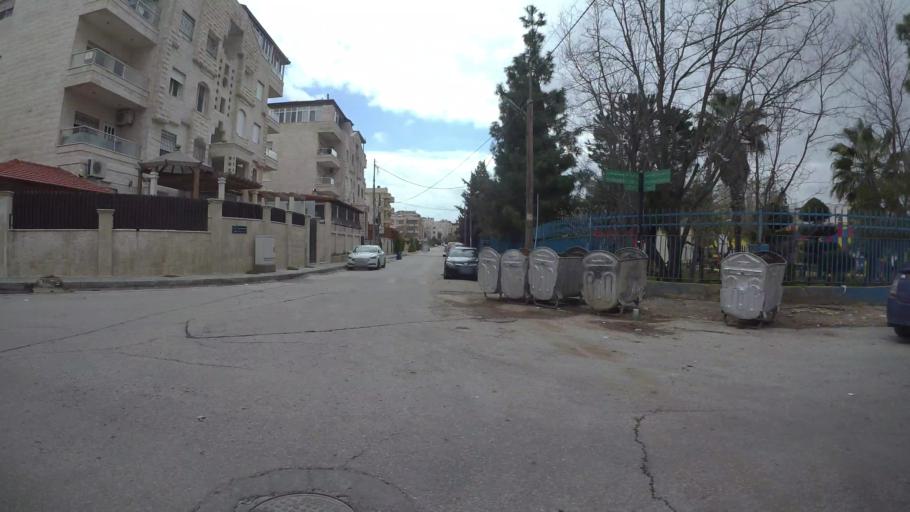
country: JO
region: Amman
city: Al Jubayhah
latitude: 31.9937
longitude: 35.8473
